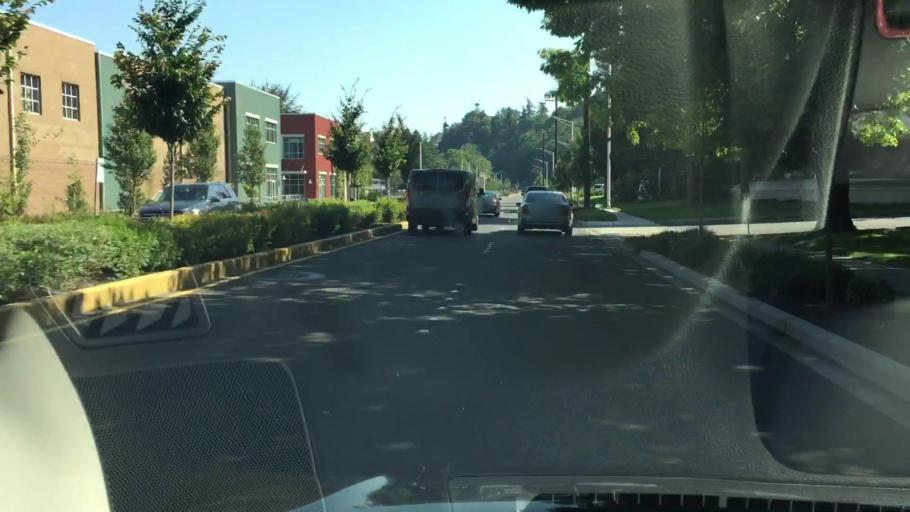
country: US
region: Washington
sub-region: King County
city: Tukwila
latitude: 47.4724
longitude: -122.2552
